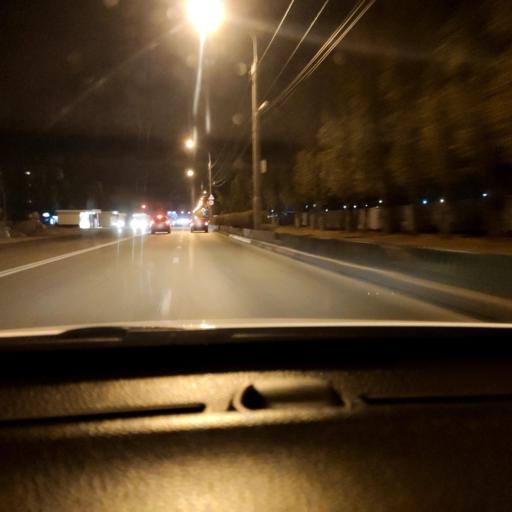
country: RU
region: Voronezj
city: Voronezh
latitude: 51.6429
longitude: 39.2666
